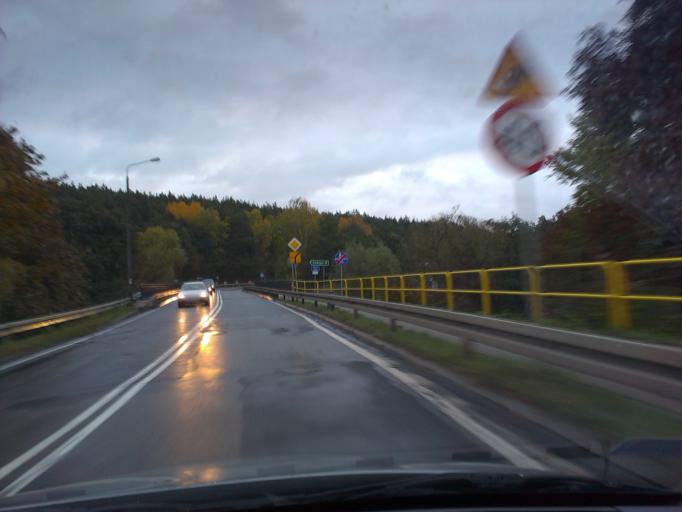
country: PL
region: Kujawsko-Pomorskie
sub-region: Powiat tucholski
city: Tuchola
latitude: 53.5640
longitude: 17.8988
